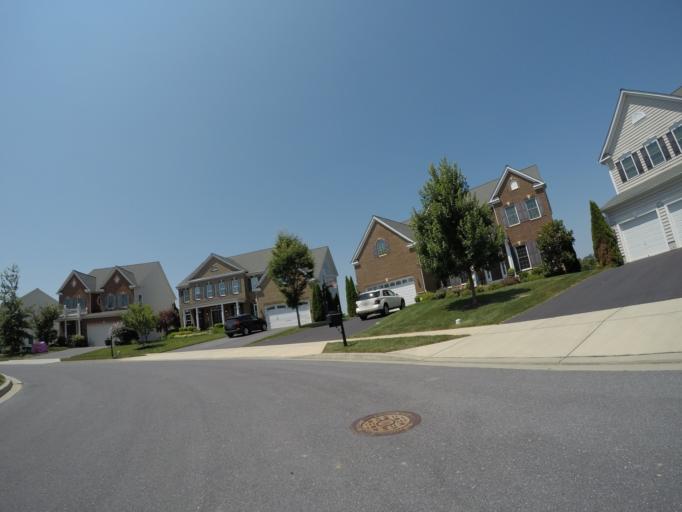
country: US
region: Maryland
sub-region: Frederick County
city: Urbana
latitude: 39.3377
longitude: -77.3596
